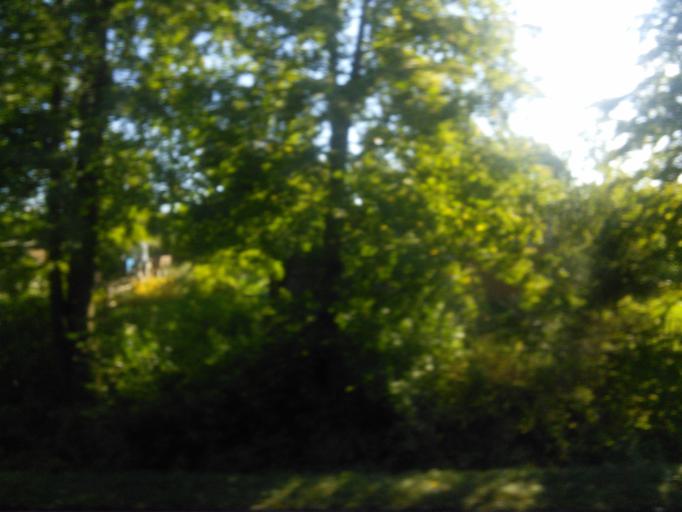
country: RU
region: Jaroslavl
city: Poshekhon'ye
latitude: 58.3755
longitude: 39.0010
